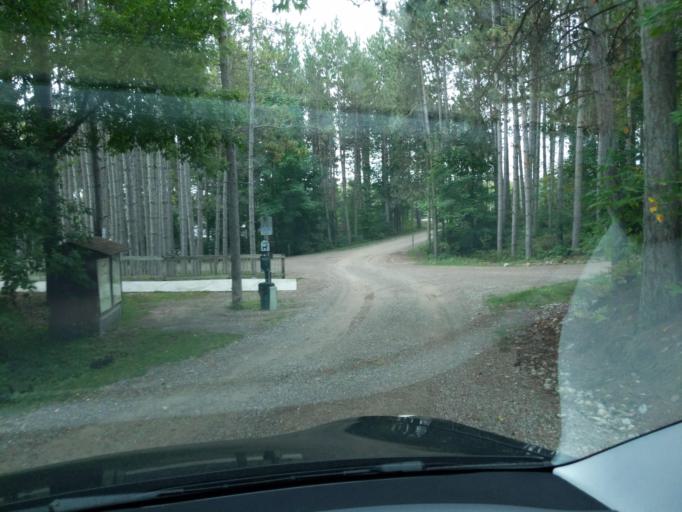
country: US
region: Michigan
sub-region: Antrim County
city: Elk Rapids
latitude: 44.8171
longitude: -85.3872
